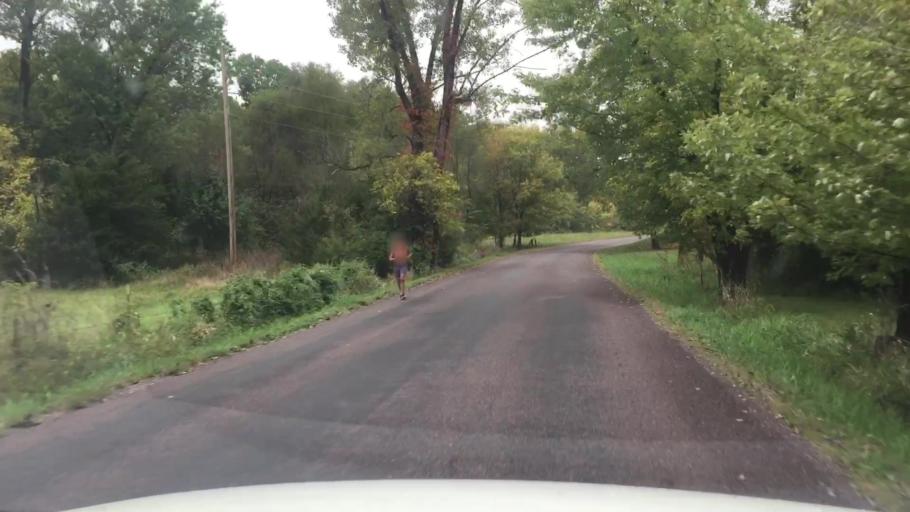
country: US
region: Missouri
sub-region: Boone County
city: Columbia
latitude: 38.8604
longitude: -92.3736
